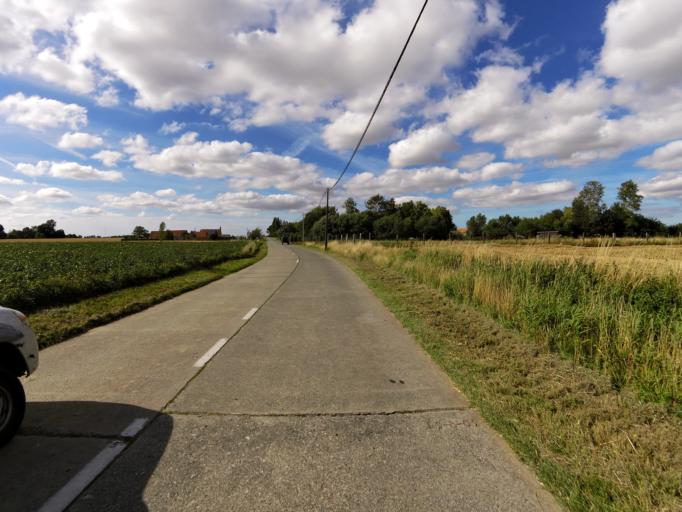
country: BE
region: Flanders
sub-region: Provincie West-Vlaanderen
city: Alveringem
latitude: 50.9722
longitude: 2.6653
